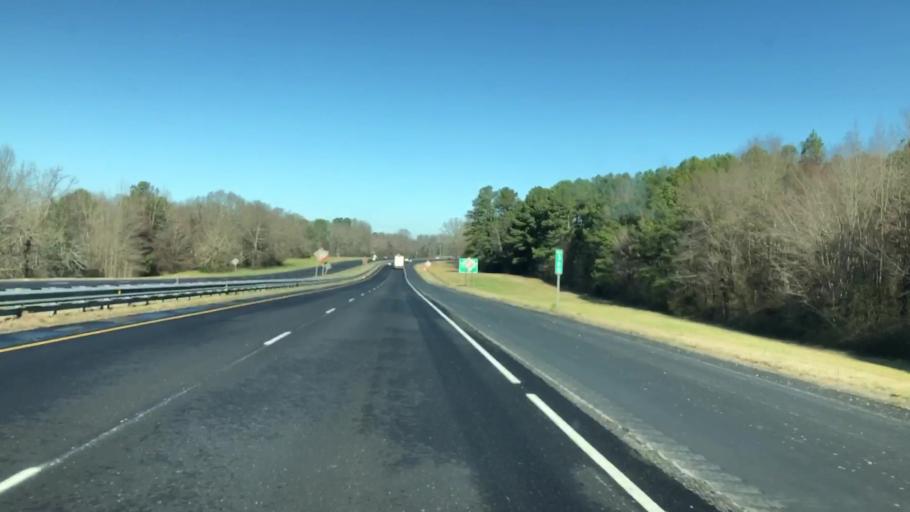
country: US
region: Alabama
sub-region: Limestone County
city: Ardmore
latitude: 34.9072
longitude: -86.9071
